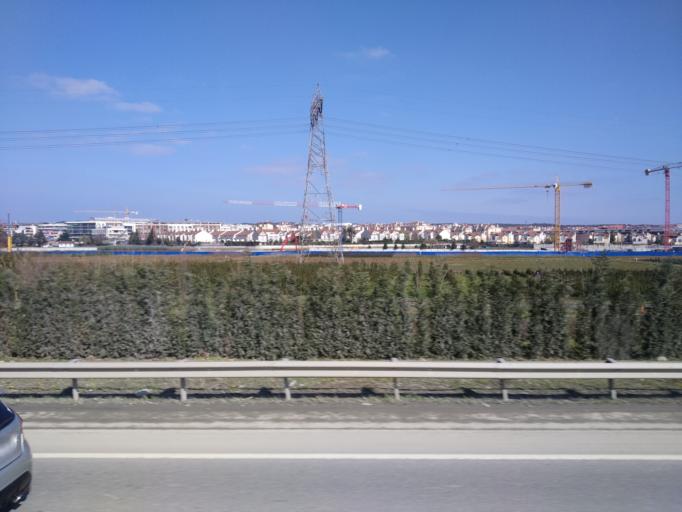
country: TR
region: Istanbul
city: Kemerburgaz
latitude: 41.1727
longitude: 28.8837
